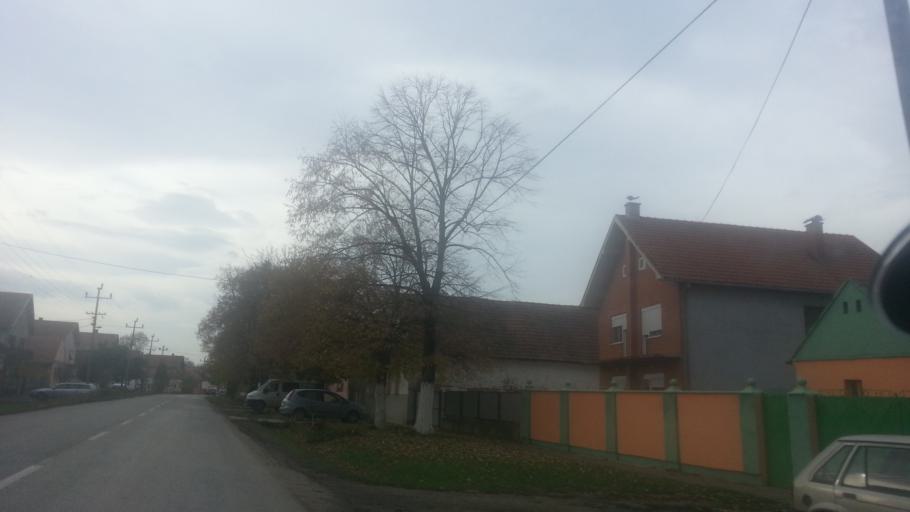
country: RS
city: Putinci
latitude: 44.9917
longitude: 19.9792
